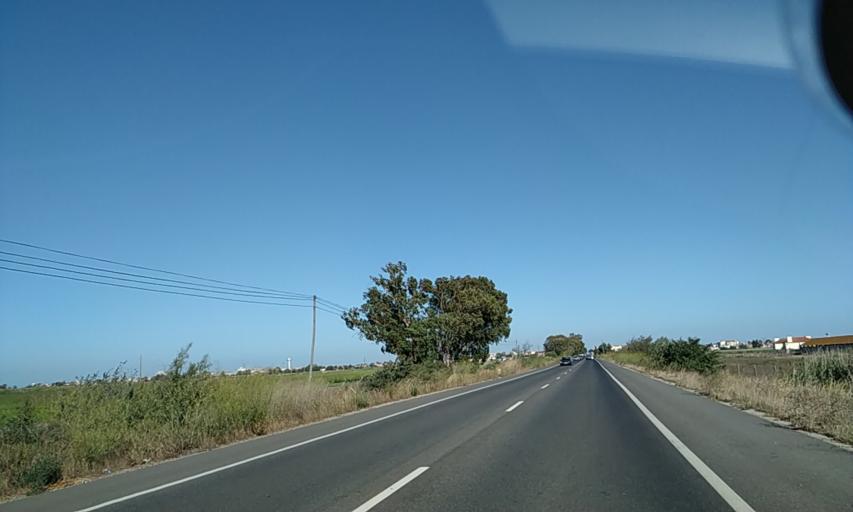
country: PT
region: Santarem
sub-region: Benavente
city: Samora Correia
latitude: 38.9295
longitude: -8.9062
